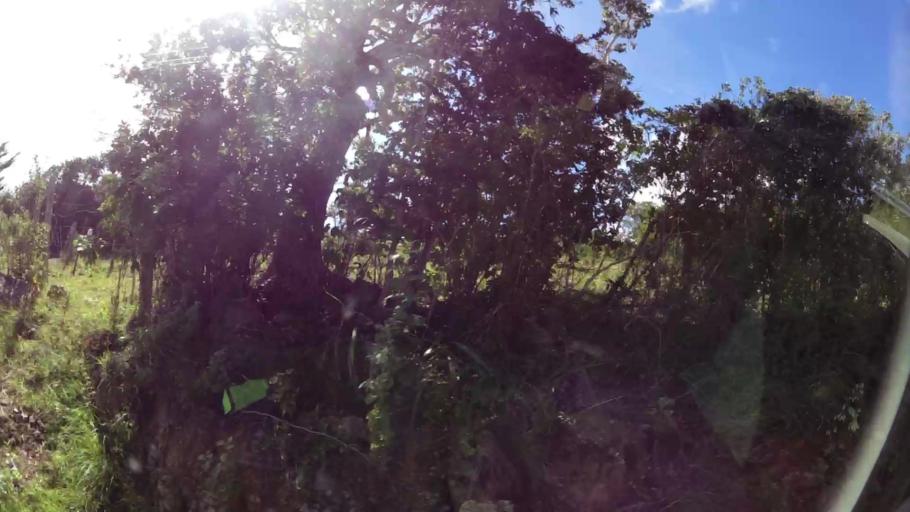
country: VG
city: Tortola
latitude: 18.4880
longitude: -64.3974
